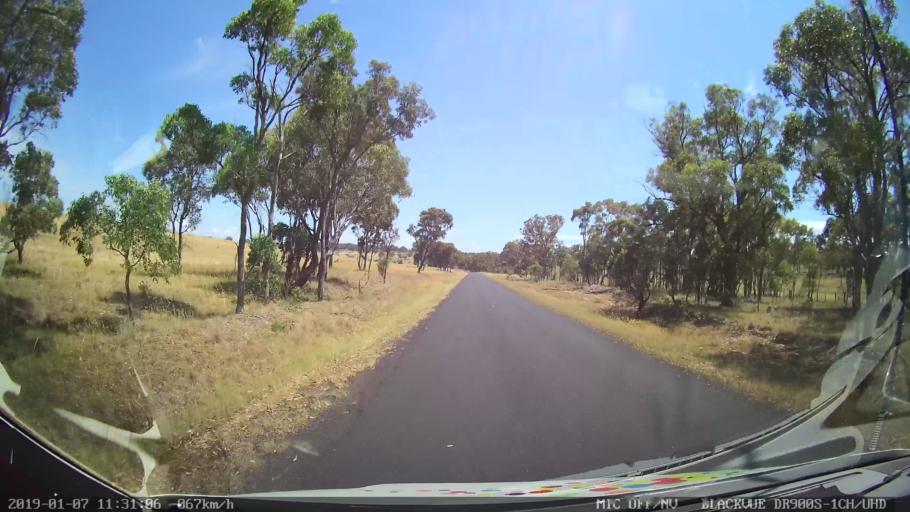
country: AU
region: New South Wales
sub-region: Armidale Dumaresq
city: Armidale
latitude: -30.4231
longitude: 151.5636
